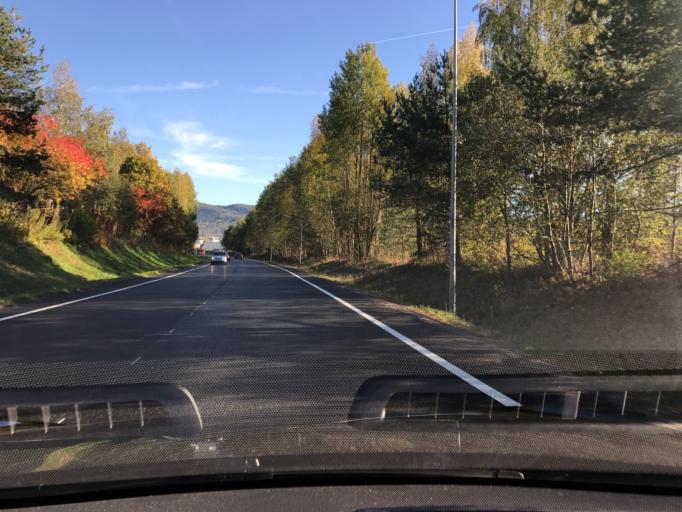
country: NO
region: Buskerud
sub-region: Nedre Eiker
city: Mjondalen
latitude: 59.7591
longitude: 9.9865
